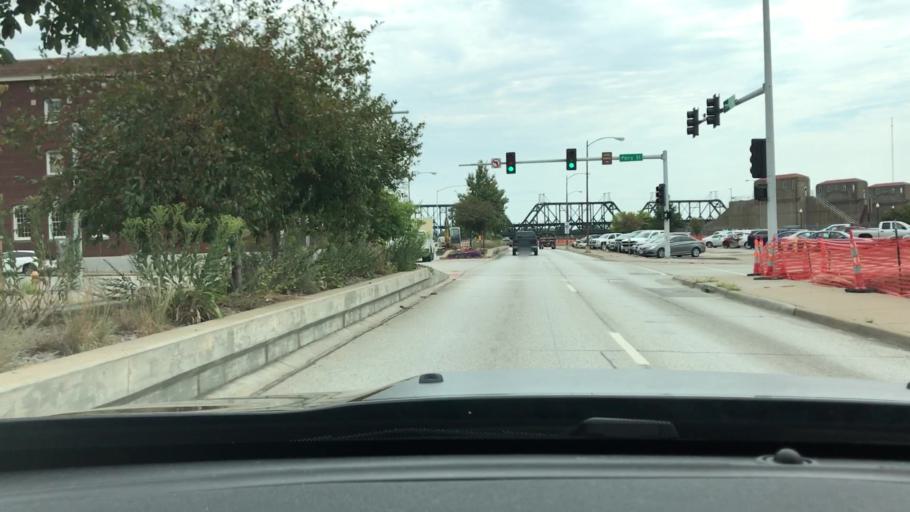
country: US
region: Iowa
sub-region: Scott County
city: Davenport
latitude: 41.5202
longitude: -90.5731
